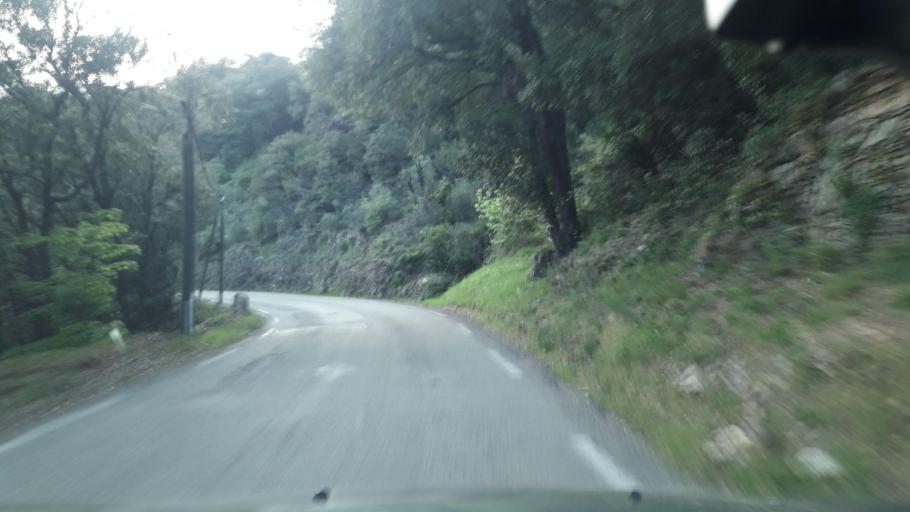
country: FR
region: Languedoc-Roussillon
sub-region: Departement du Gard
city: Valleraugue
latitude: 44.1272
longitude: 3.7460
